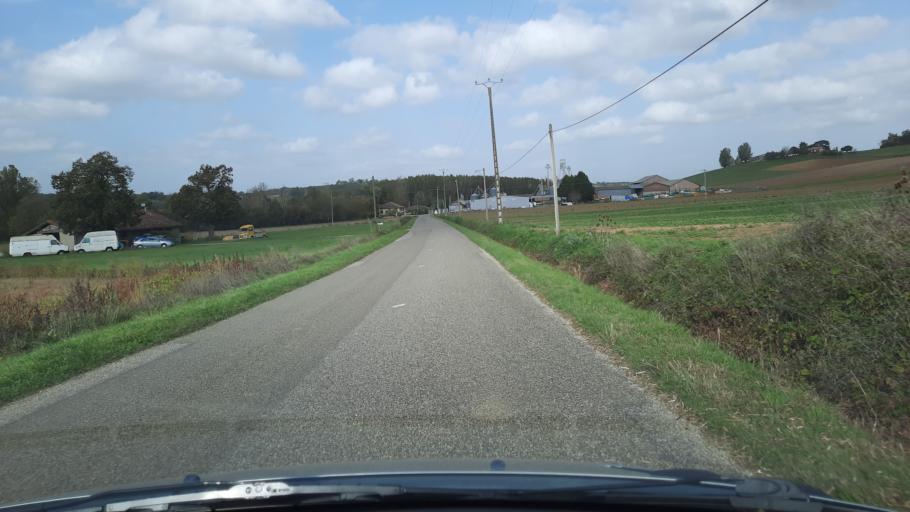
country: FR
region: Midi-Pyrenees
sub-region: Departement du Tarn-et-Garonne
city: Lafrancaise
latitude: 44.1730
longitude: 1.2761
